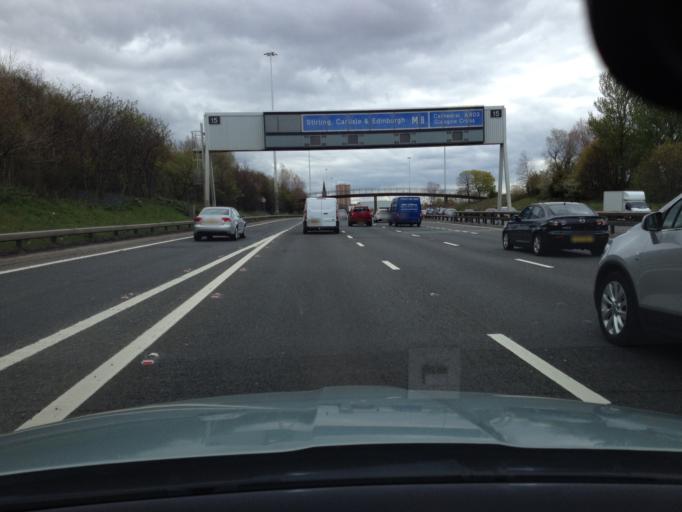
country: GB
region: Scotland
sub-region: Glasgow City
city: Glasgow
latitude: 55.8700
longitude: -4.2476
